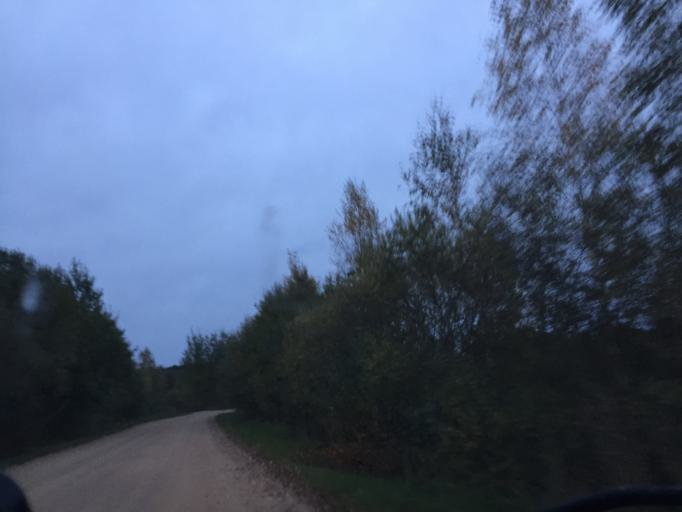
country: LV
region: Garkalne
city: Garkalne
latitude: 57.0816
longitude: 24.3792
